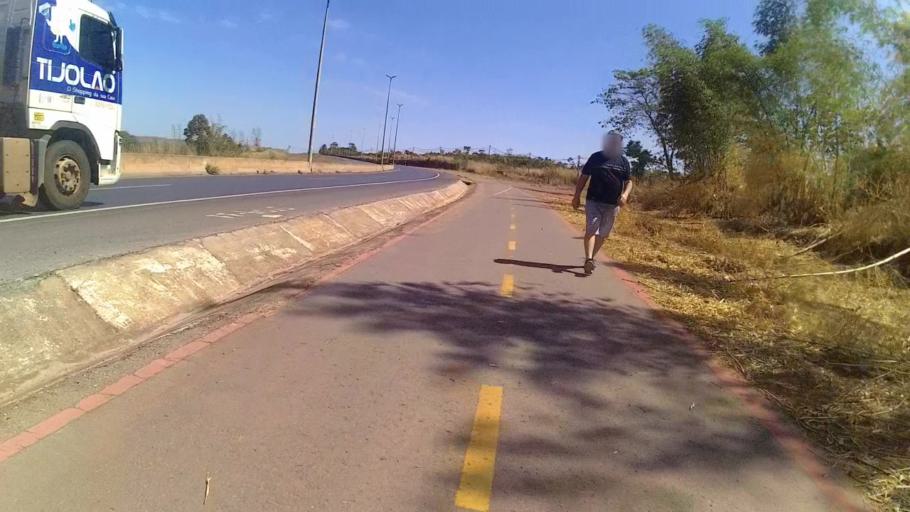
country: BR
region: Federal District
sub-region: Brasilia
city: Brasilia
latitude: -15.6535
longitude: -47.8461
